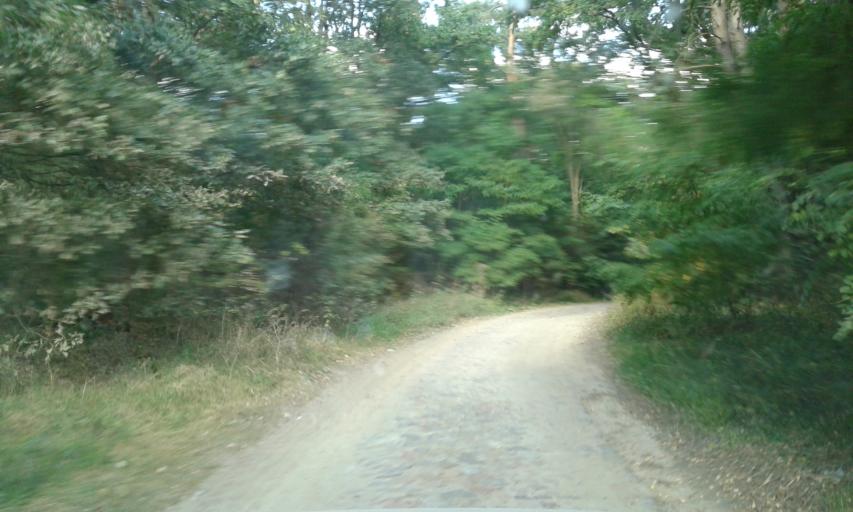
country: PL
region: West Pomeranian Voivodeship
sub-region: Powiat stargardzki
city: Dolice
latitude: 53.2452
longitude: 15.2231
